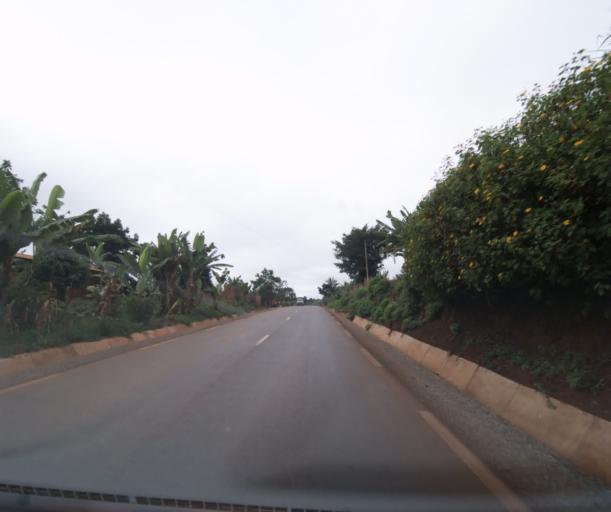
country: CM
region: West
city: Mbouda
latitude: 5.5675
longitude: 10.3113
